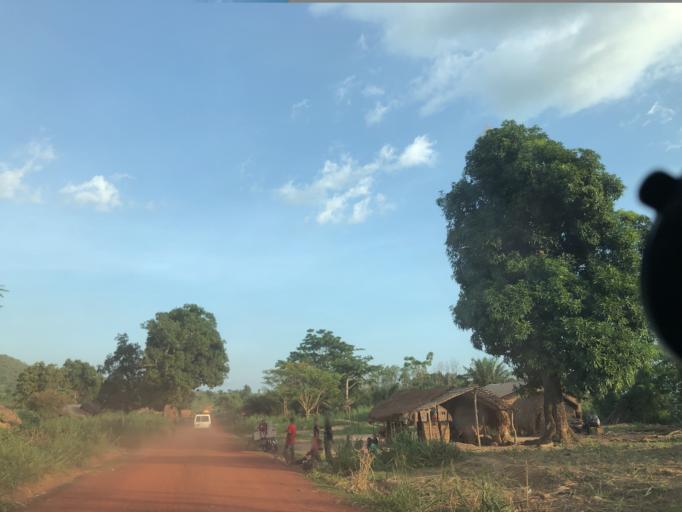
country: CF
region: Bangui
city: Bangui
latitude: 4.2895
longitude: 18.6203
